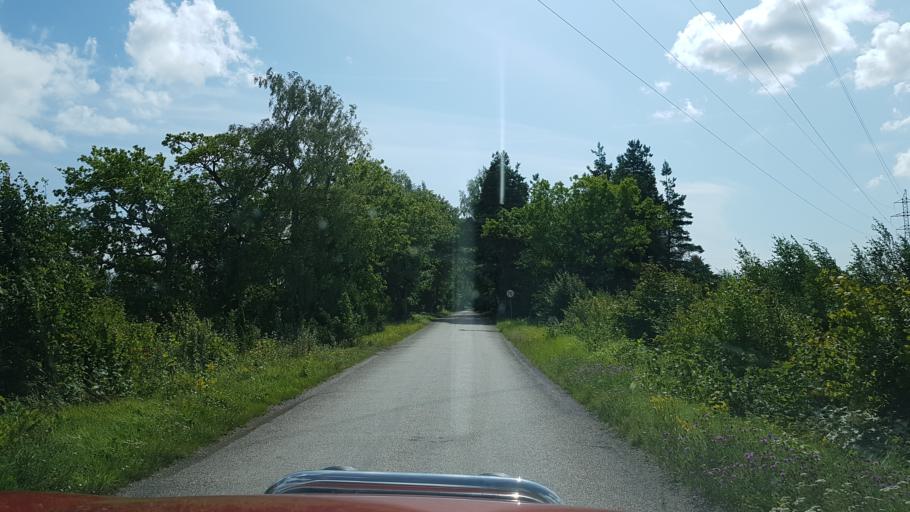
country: EE
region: Laeaene
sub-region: Lihula vald
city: Lihula
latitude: 58.5864
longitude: 23.5374
